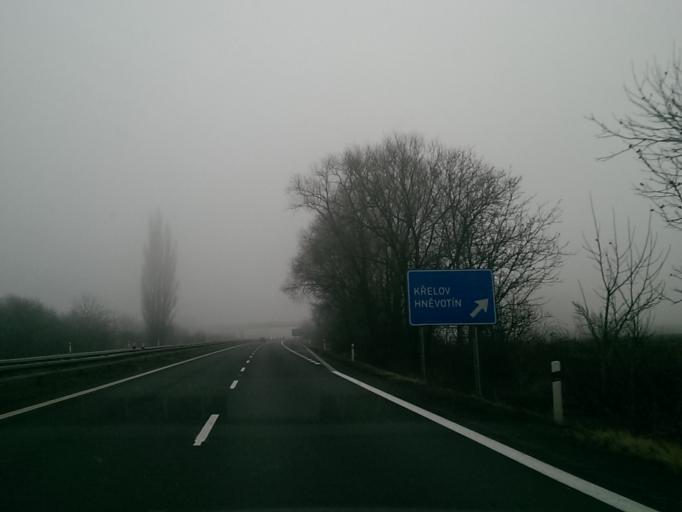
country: CZ
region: Olomoucky
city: Skrben
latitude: 49.6163
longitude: 17.1862
